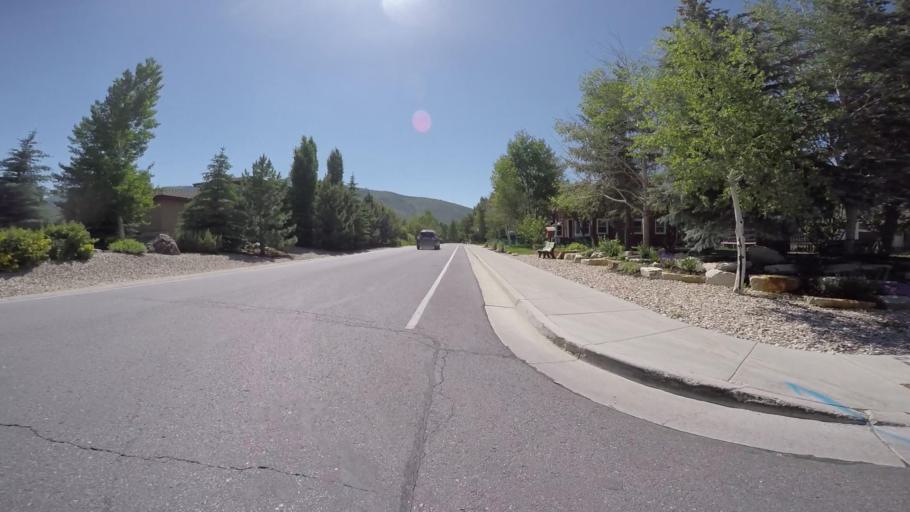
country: US
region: Utah
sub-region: Summit County
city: Park City
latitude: 40.6719
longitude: -111.5066
